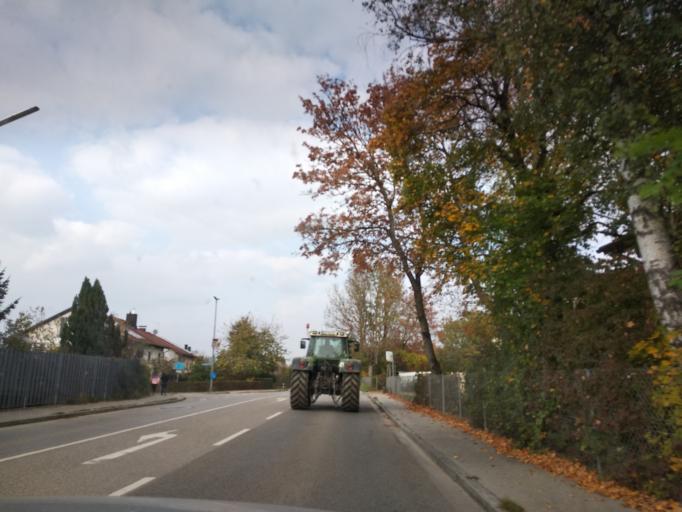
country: DE
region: Bavaria
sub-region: Upper Bavaria
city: Markt Schwaben
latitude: 48.1959
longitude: 11.8751
